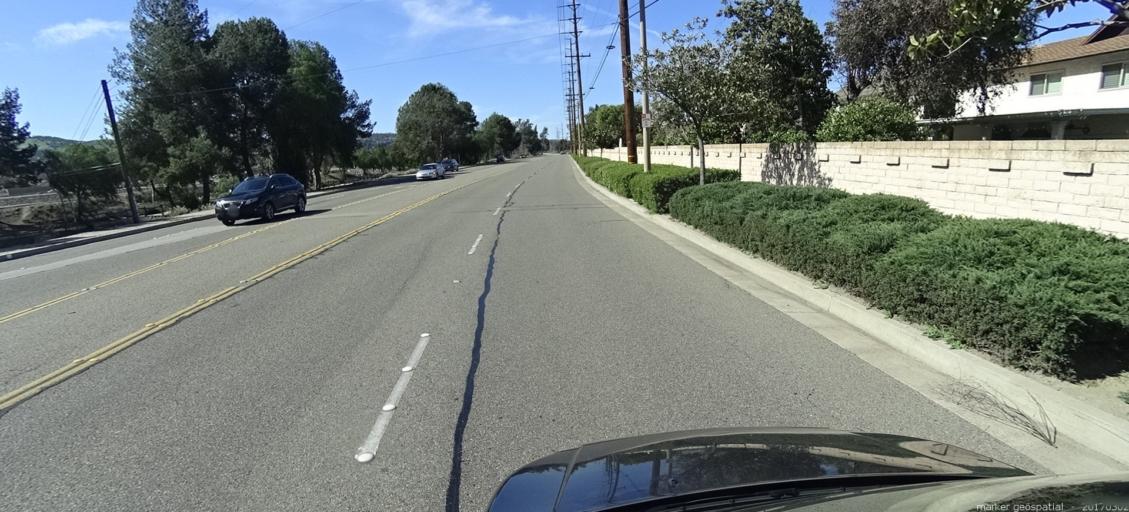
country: US
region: California
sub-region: Orange County
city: Yorba Linda
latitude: 33.8628
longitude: -117.7770
